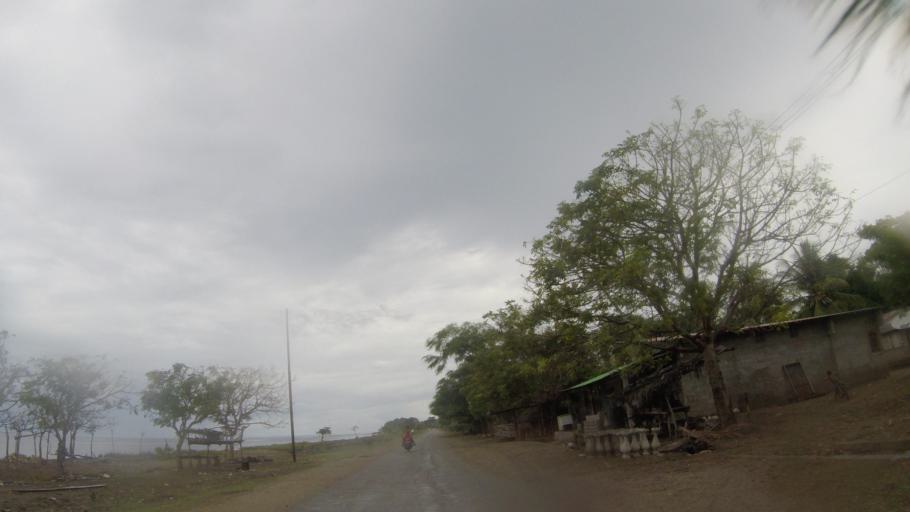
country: TL
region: Lautem
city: Lospalos
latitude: -8.3541
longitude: 126.9144
